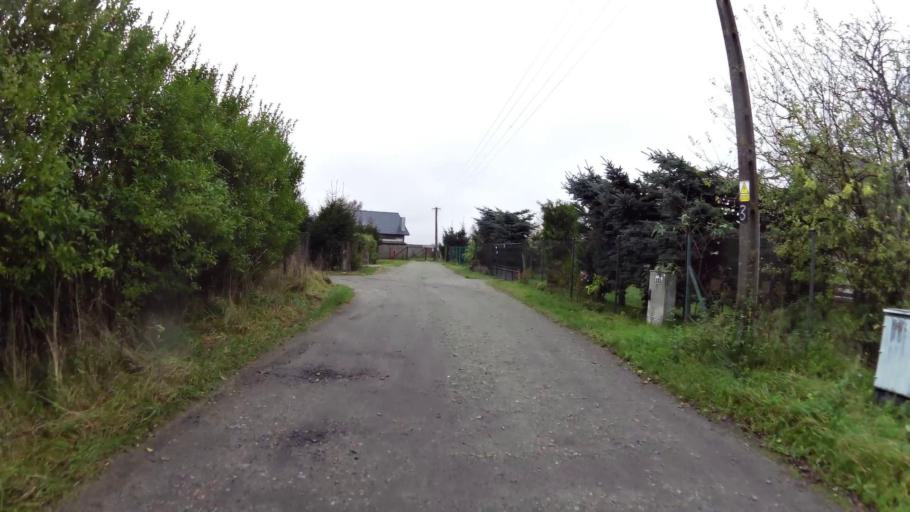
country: PL
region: West Pomeranian Voivodeship
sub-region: Powiat koszalinski
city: Mielno
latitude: 54.2547
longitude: 16.0947
